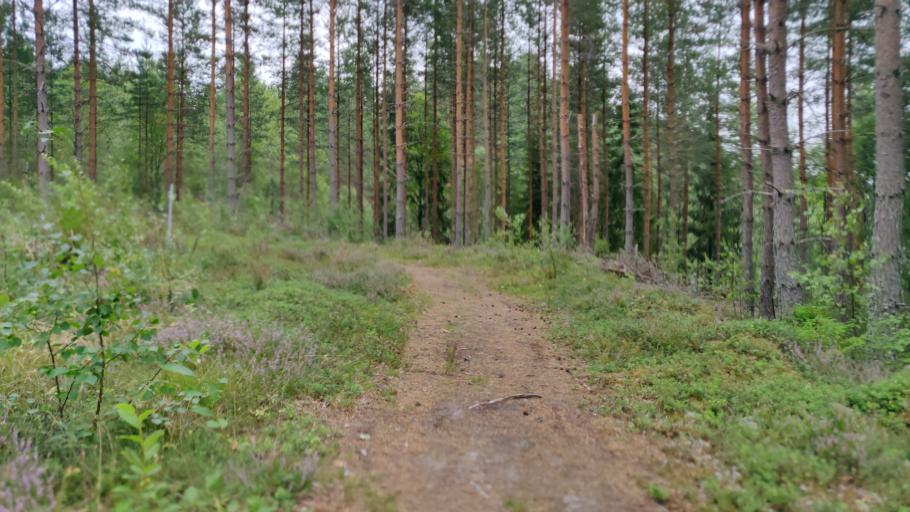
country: SE
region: Vaermland
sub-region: Hagfors Kommun
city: Hagfors
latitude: 60.0197
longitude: 13.5578
